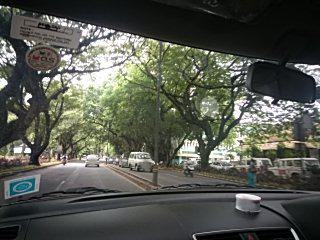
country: IN
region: Goa
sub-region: North Goa
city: Panaji
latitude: 15.4967
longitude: 73.8192
